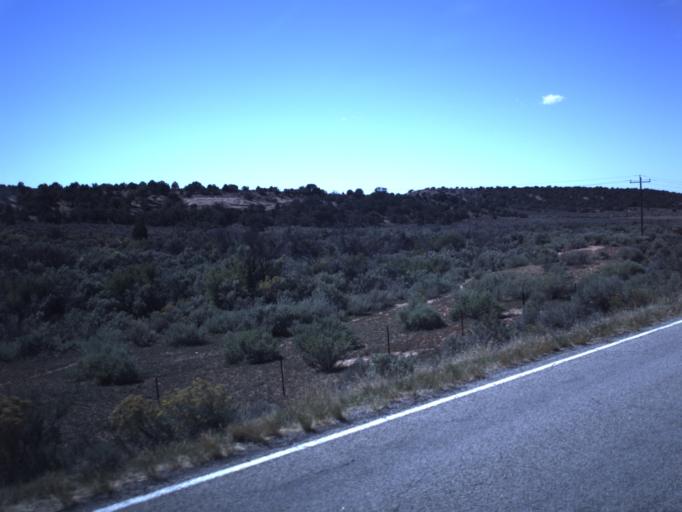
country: US
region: Utah
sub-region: Grand County
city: Moab
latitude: 38.3044
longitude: -109.3856
